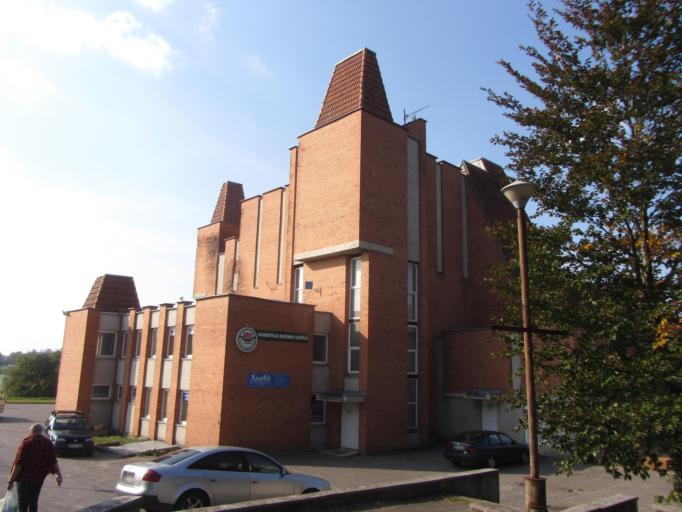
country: LT
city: Trakai
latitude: 54.6380
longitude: 24.9340
